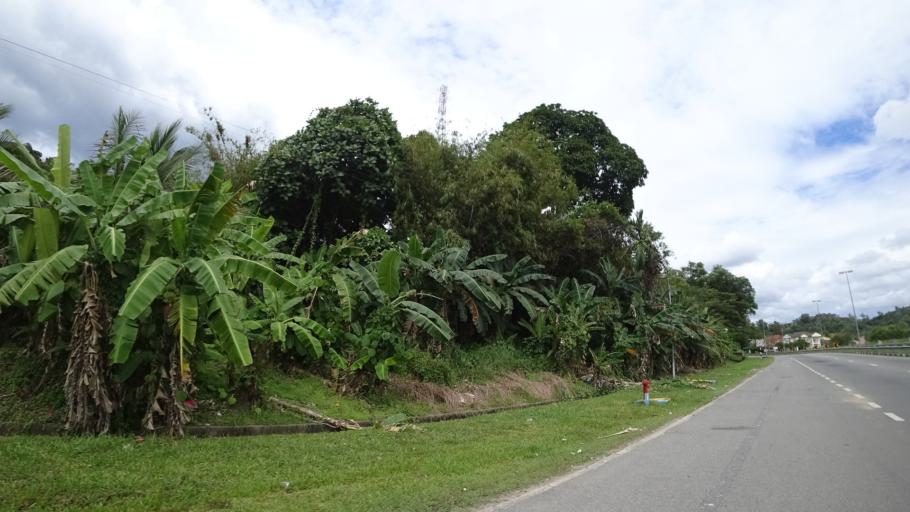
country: BN
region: Brunei and Muara
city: Bandar Seri Begawan
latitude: 4.8803
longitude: 114.8771
